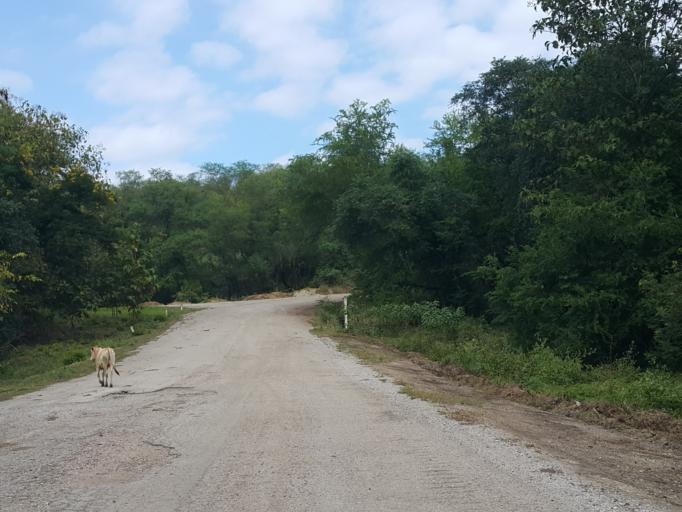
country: TH
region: Lampang
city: Mae Mo
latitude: 18.3261
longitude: 99.7518
